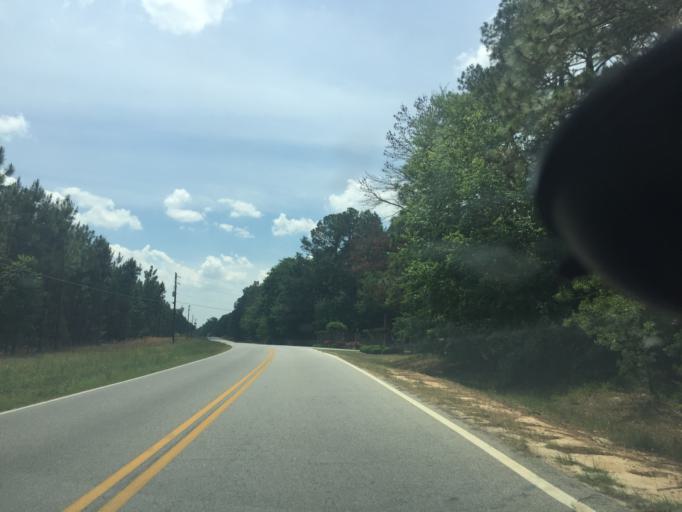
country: US
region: Georgia
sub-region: Bulloch County
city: Statesboro
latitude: 32.4129
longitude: -81.8282
